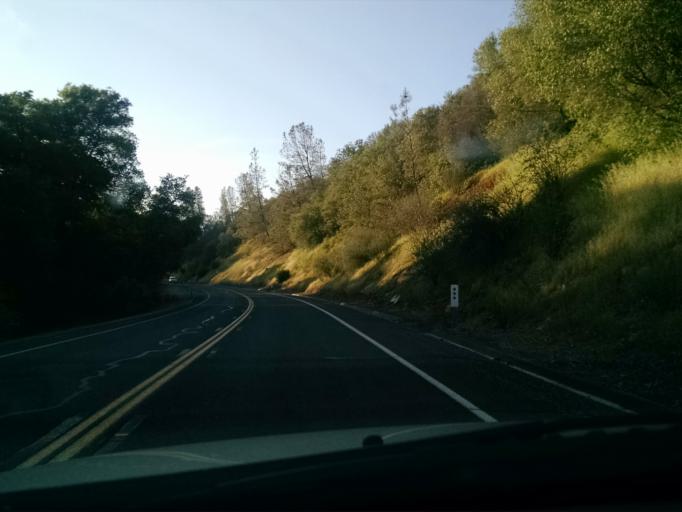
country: US
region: California
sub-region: Mariposa County
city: Mariposa
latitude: 37.4726
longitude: -119.9534
